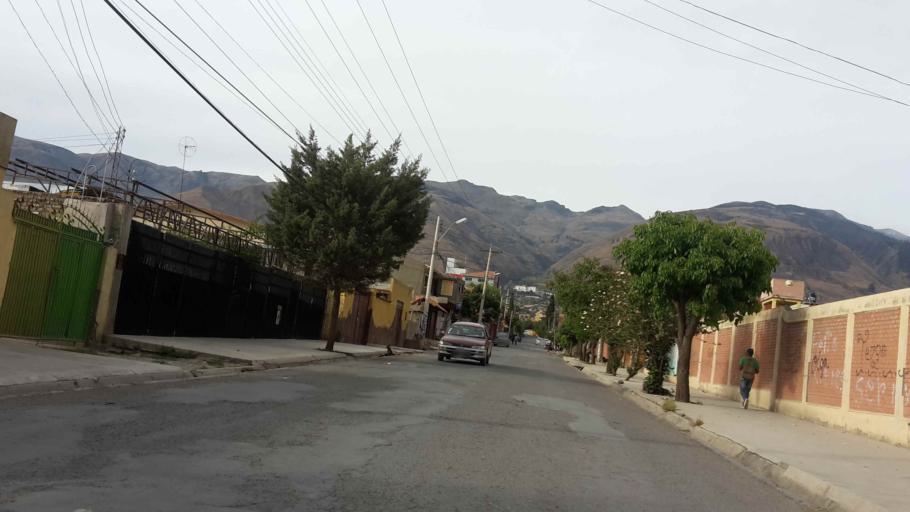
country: BO
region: Cochabamba
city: Cochabamba
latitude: -17.3557
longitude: -66.1948
